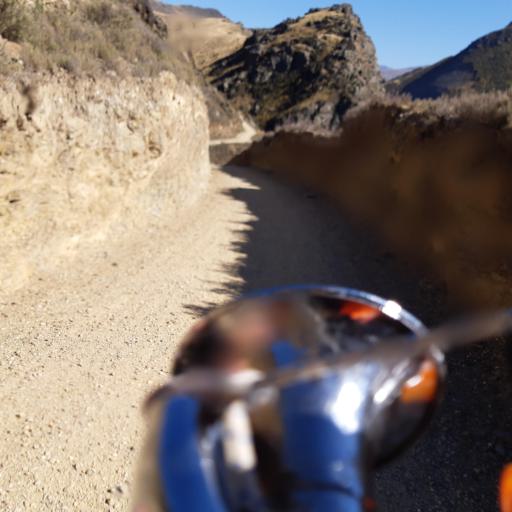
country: NZ
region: Otago
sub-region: Queenstown-Lakes District
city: Wanaka
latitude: -45.0853
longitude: 169.2528
